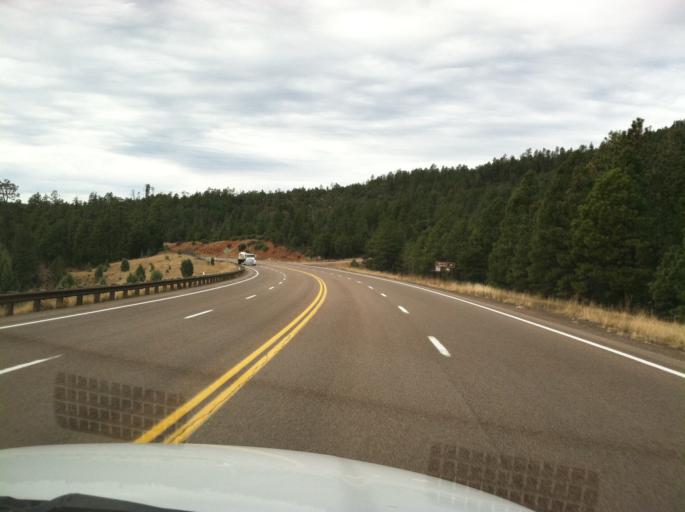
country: US
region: Arizona
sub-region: Gila County
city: Star Valley
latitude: 34.3062
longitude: -110.9474
